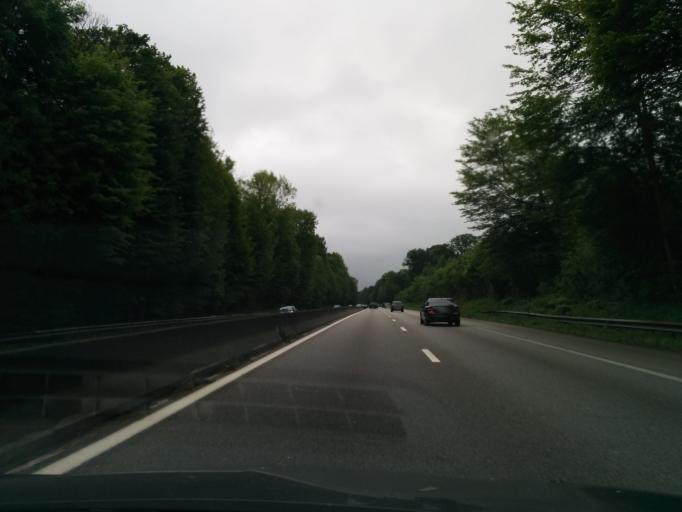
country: FR
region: Ile-de-France
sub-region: Departement des Yvelines
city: Saint-Nom-la-Breteche
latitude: 48.8906
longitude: 2.0096
